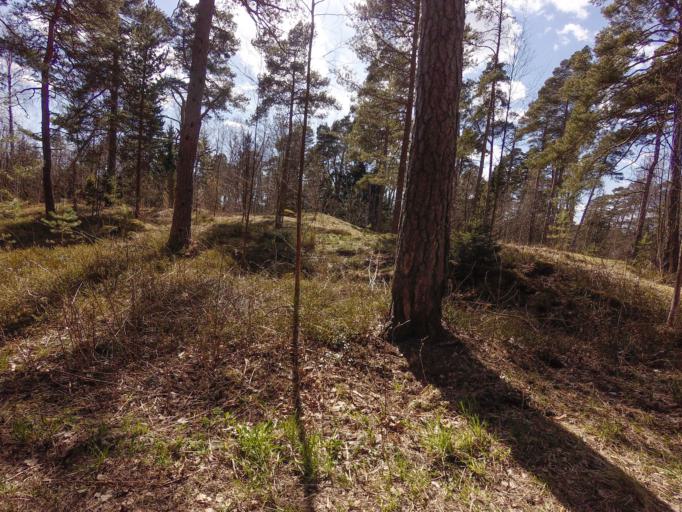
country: FI
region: Uusimaa
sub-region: Helsinki
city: Helsinki
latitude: 60.1655
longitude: 25.0372
